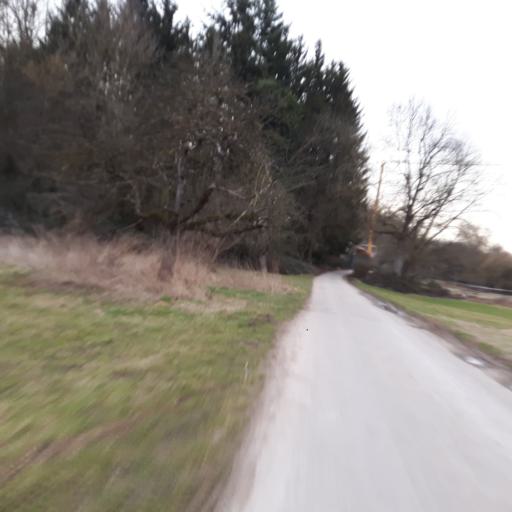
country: DE
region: Baden-Wuerttemberg
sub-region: Regierungsbezirk Stuttgart
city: Freiberg am Neckar
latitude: 48.9433
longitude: 9.1852
